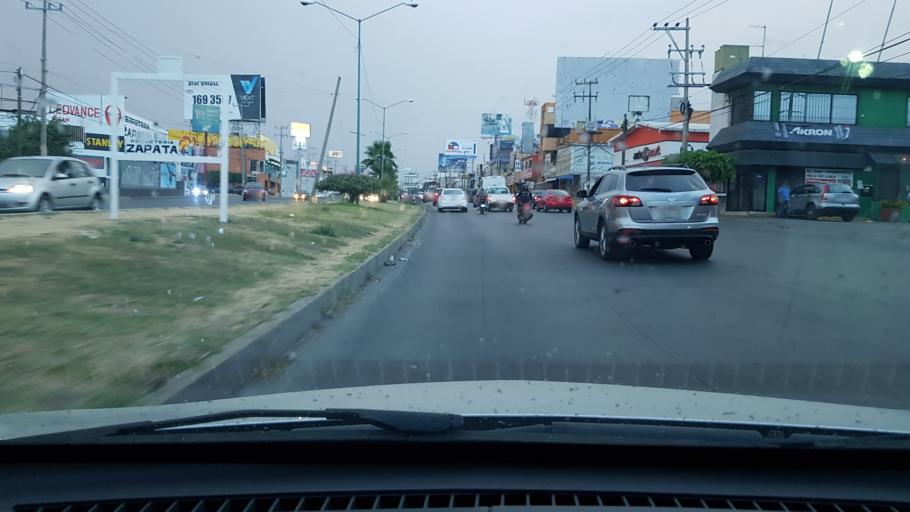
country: MX
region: Morelos
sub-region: Tepoztlan
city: Loma Bonita
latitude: 18.9115
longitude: -99.1815
